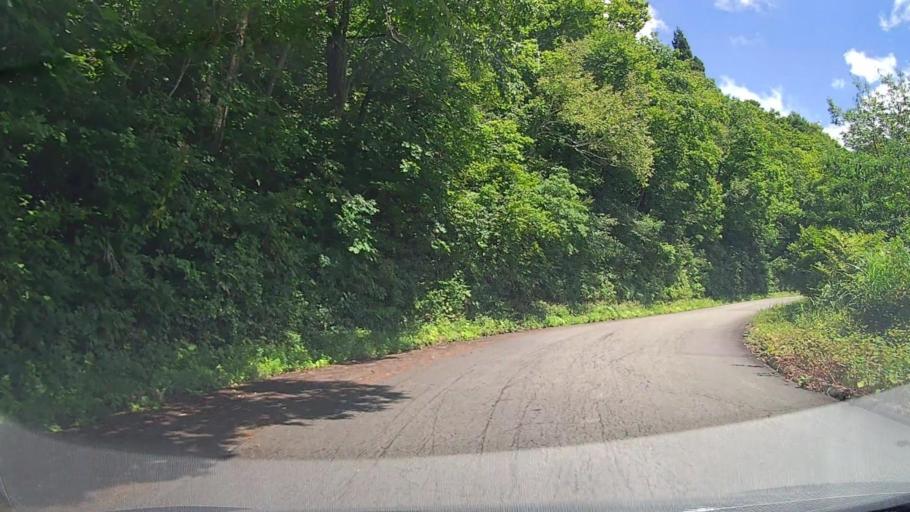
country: JP
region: Nagano
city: Iiyama
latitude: 36.9345
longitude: 138.4544
